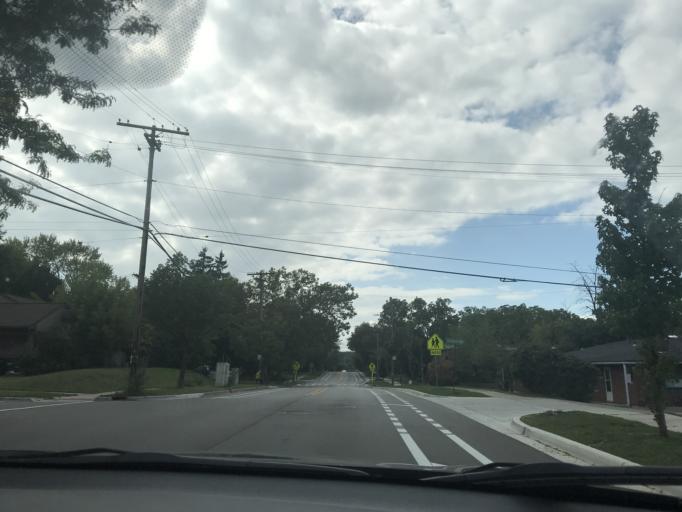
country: US
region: Michigan
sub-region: Washtenaw County
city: Ann Arbor
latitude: 42.2682
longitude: -83.7661
